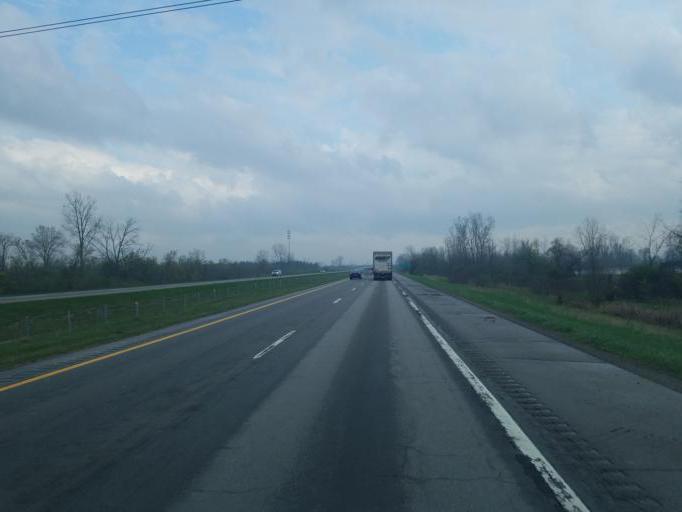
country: US
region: Michigan
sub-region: Washtenaw County
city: Milan
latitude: 42.1204
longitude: -83.6830
